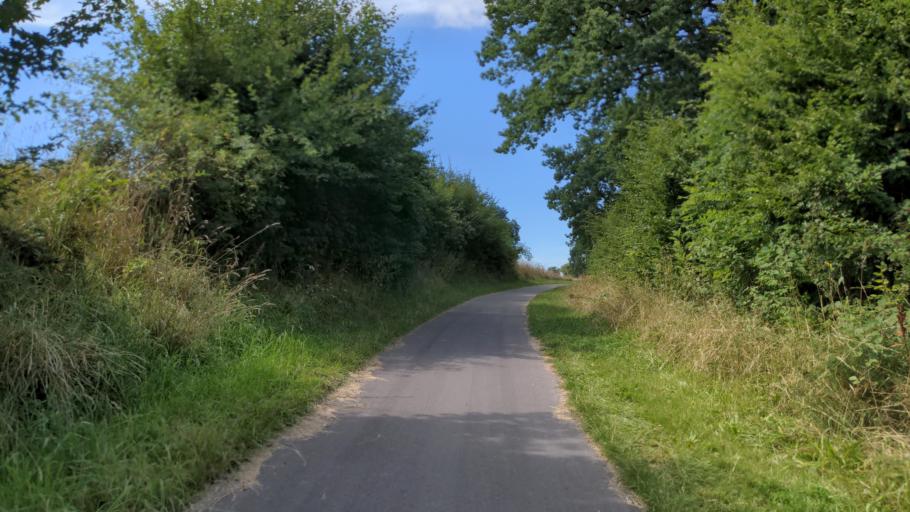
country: DE
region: Schleswig-Holstein
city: Grebin
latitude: 54.1855
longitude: 10.5288
